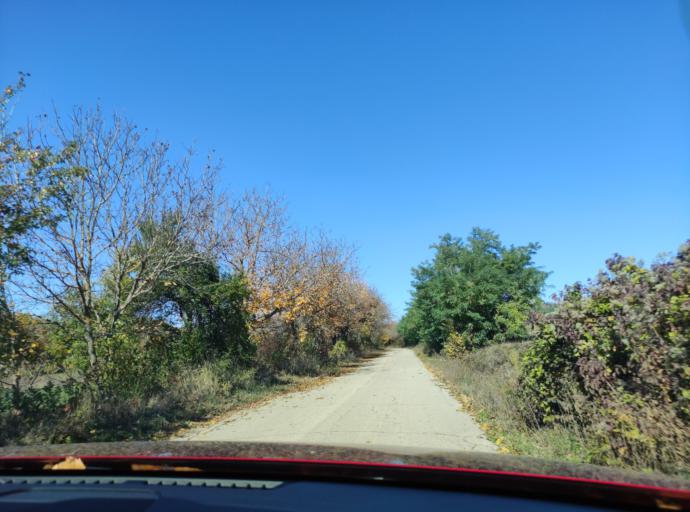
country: BG
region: Montana
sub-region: Obshtina Montana
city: Montana
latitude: 43.4278
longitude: 23.0638
